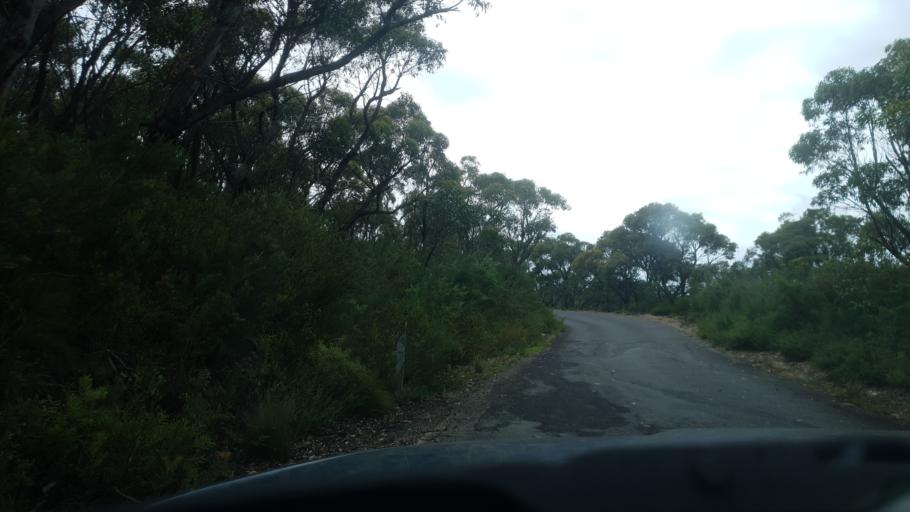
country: AU
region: Victoria
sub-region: Northern Grampians
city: Stawell
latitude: -37.2640
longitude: 142.5755
